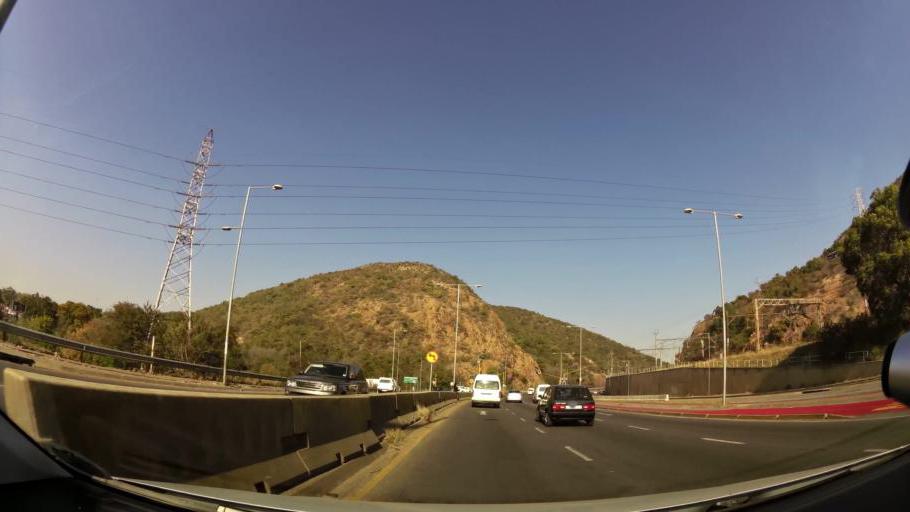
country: ZA
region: Gauteng
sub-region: City of Tshwane Metropolitan Municipality
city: Pretoria
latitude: -25.6873
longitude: 28.1862
